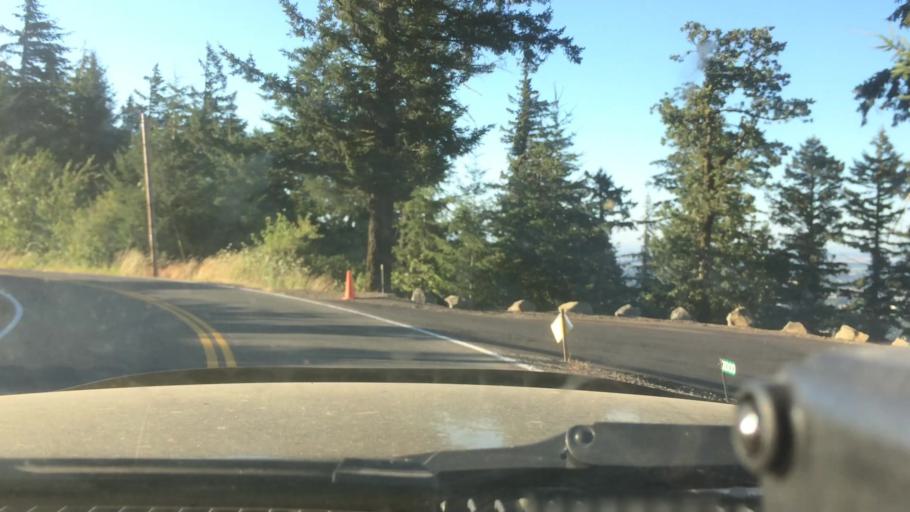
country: US
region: Oregon
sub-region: Yamhill County
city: Newberg
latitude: 45.3382
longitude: -122.9467
